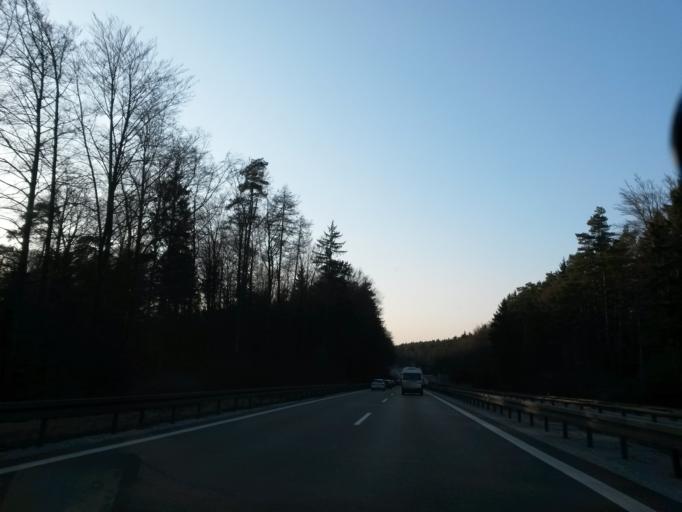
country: DE
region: Bavaria
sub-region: Upper Bavaria
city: Denkendorf
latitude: 48.9732
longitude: 11.4064
